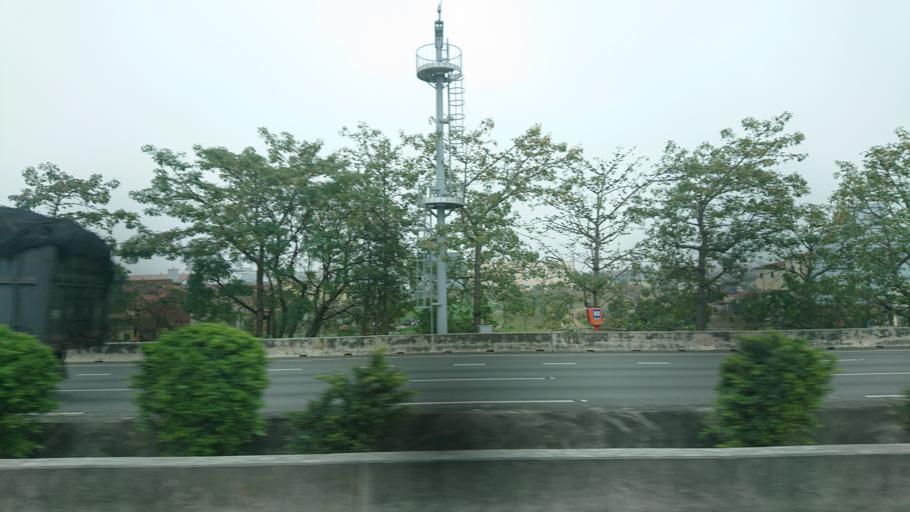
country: TW
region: Taiwan
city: Fengyuan
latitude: 24.2782
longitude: 120.6938
